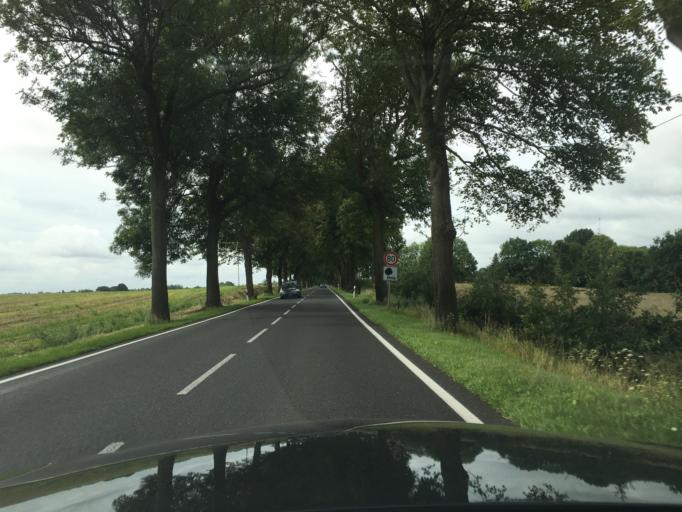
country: DE
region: Brandenburg
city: Gransee
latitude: 52.9094
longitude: 13.1585
